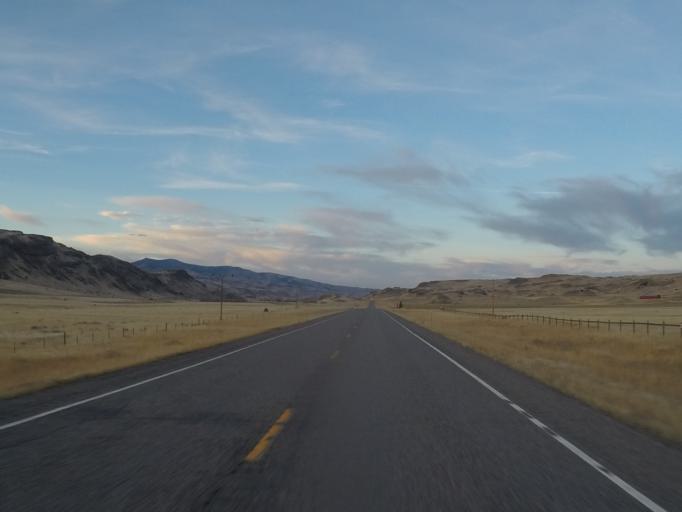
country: US
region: Montana
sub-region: Gallatin County
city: Bozeman
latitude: 45.2240
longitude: -110.8806
